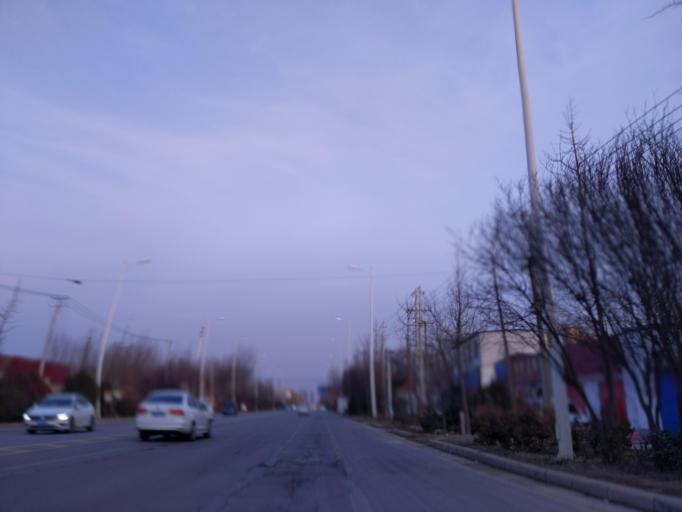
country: CN
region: Henan Sheng
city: Zhongyuanlu
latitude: 35.7869
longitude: 115.1238
